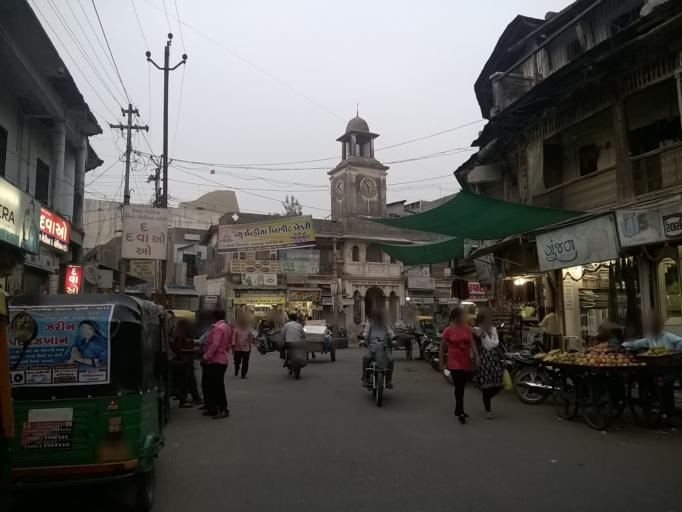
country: IN
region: Gujarat
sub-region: Kheda
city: Nadiad
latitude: 22.6959
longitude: 72.8603
